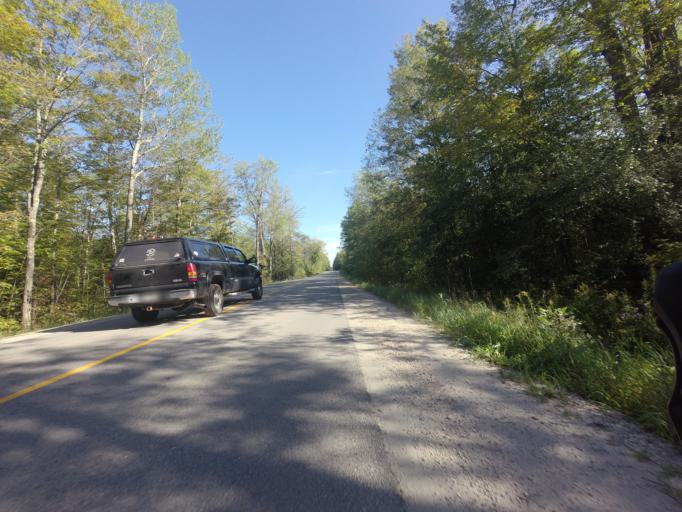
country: CA
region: Ontario
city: Perth
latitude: 44.8995
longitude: -76.3294
